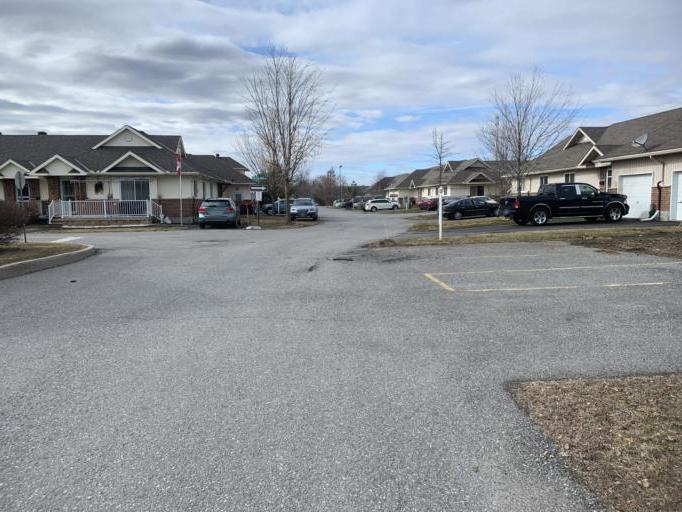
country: CA
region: Ontario
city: Bells Corners
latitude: 45.1944
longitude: -75.8410
